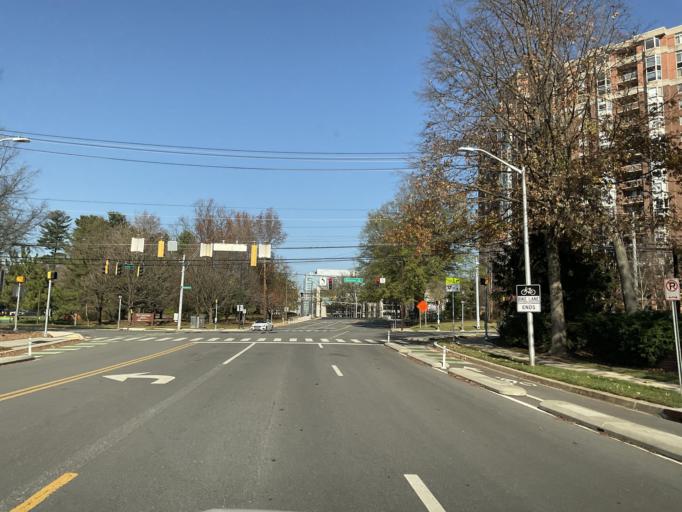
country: US
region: Maryland
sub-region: Montgomery County
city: North Bethesda
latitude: 39.0445
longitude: -77.1168
